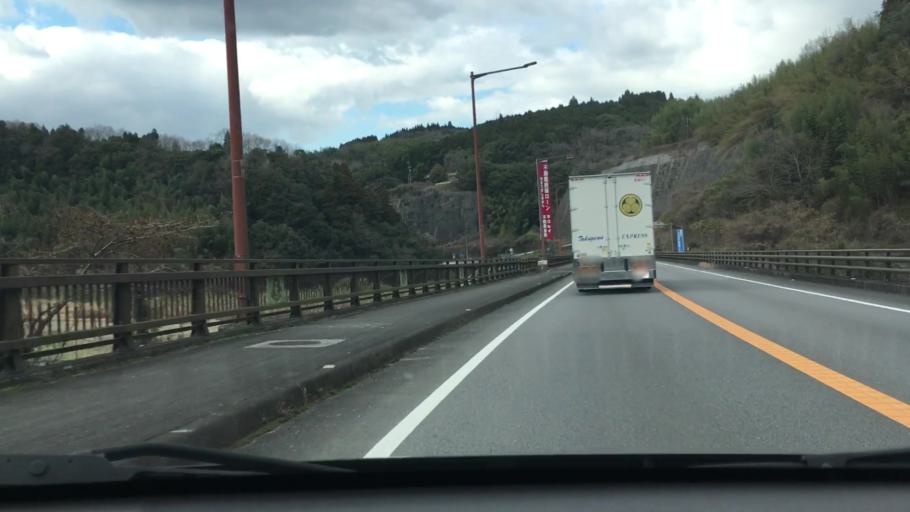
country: JP
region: Oita
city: Usuki
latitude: 33.0668
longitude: 131.6563
